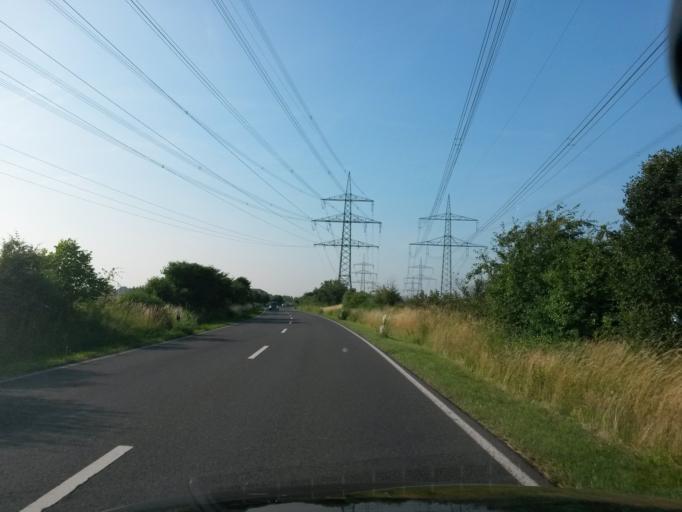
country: DE
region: North Rhine-Westphalia
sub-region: Regierungsbezirk Koln
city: Alfter
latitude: 50.7276
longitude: 7.0338
